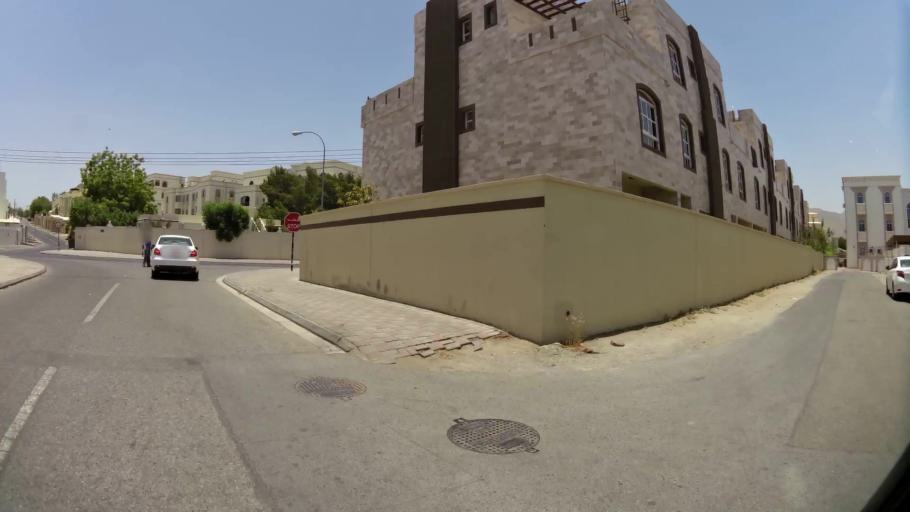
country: OM
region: Muhafazat Masqat
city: Bawshar
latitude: 23.6009
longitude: 58.4493
